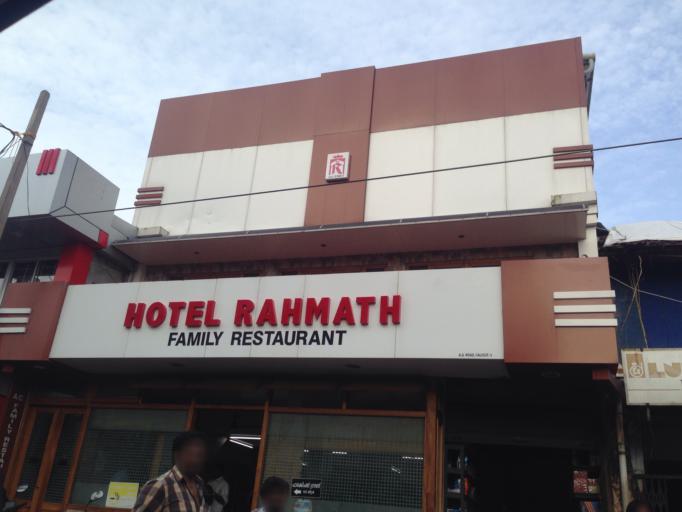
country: IN
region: Kerala
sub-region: Kozhikode
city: Kozhikode
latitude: 11.2516
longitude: 75.7791
